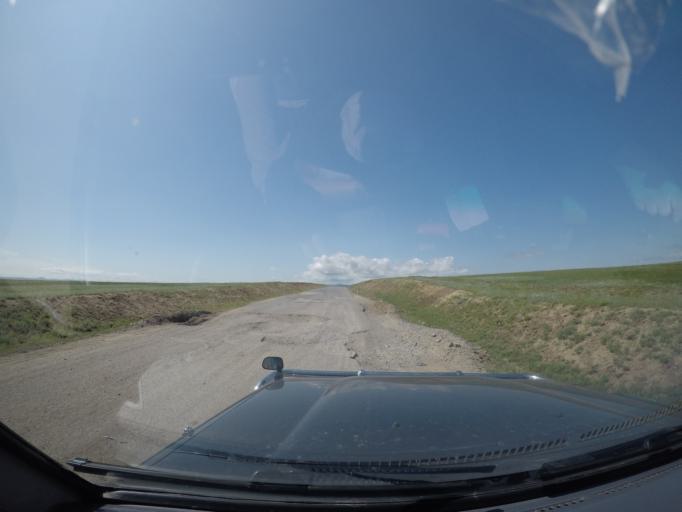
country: MN
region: Hentiy
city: Bayan
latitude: 47.2932
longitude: 111.3106
